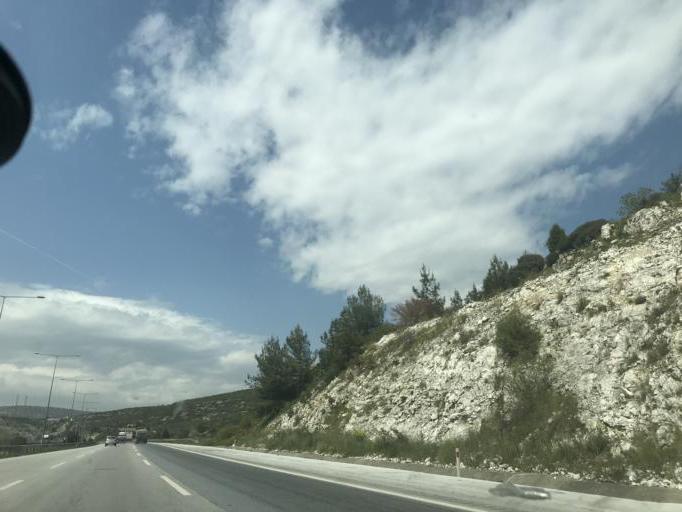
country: TR
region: Mersin
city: Tarsus
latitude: 37.1423
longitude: 34.8423
